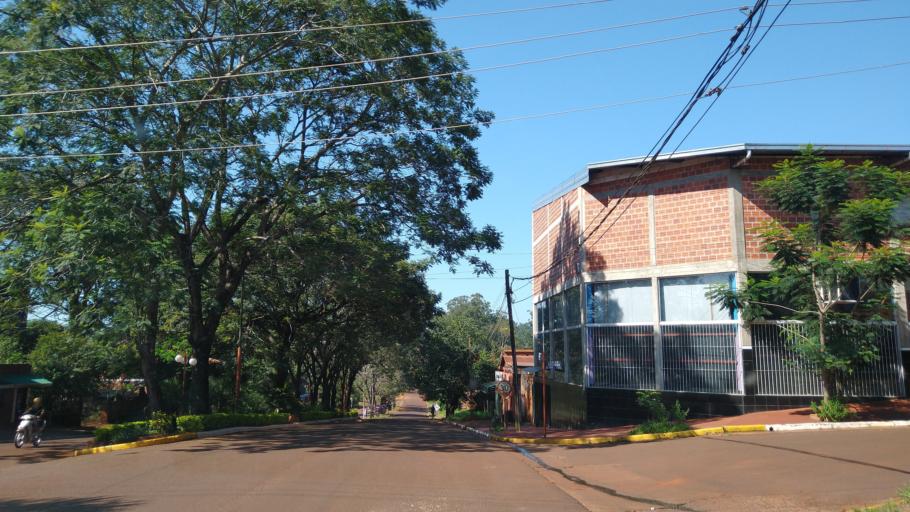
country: AR
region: Misiones
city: Puerto Esperanza
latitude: -26.0255
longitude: -54.6125
